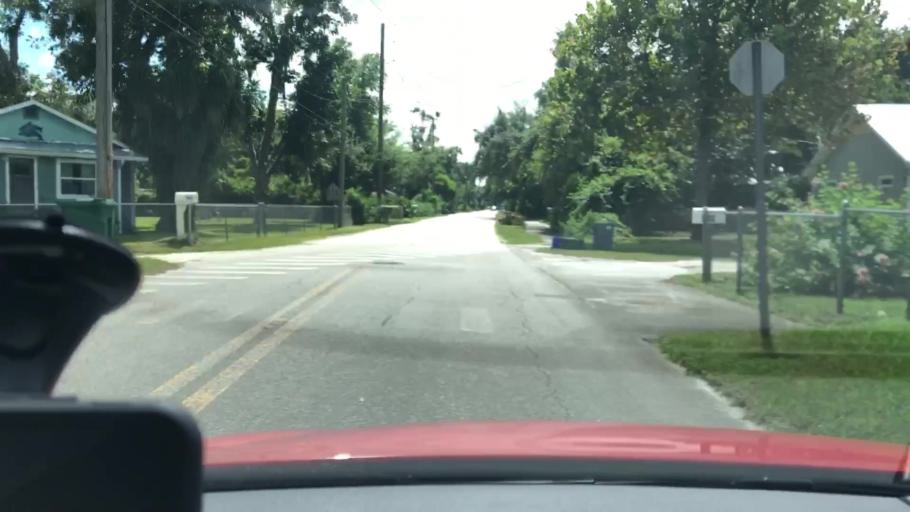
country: US
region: Florida
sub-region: Volusia County
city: New Smyrna Beach
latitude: 29.0099
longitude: -80.9249
